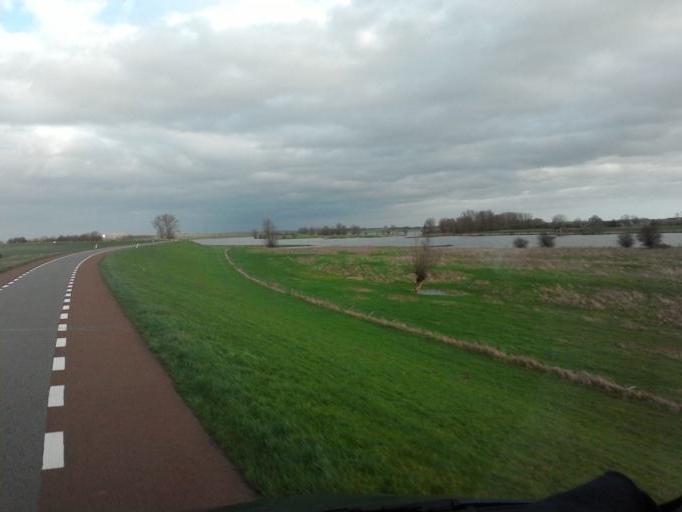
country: NL
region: Gelderland
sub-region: Gemeente Culemborg
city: Culemborg
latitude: 51.9713
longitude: 5.2221
